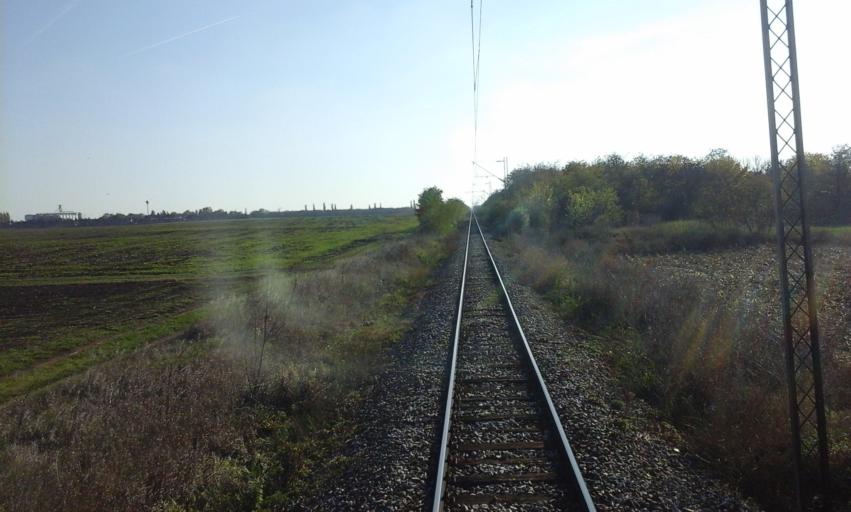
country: RS
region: Autonomna Pokrajina Vojvodina
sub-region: Severnobacki Okrug
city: Backa Topola
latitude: 45.7874
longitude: 19.6476
